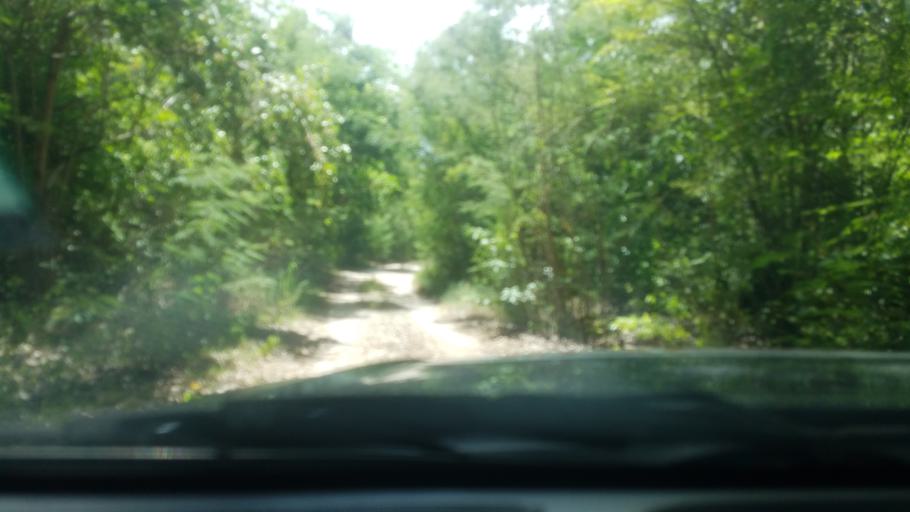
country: LC
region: Vieux-Fort
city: Vieux Fort
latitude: 13.7515
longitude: -60.9381
